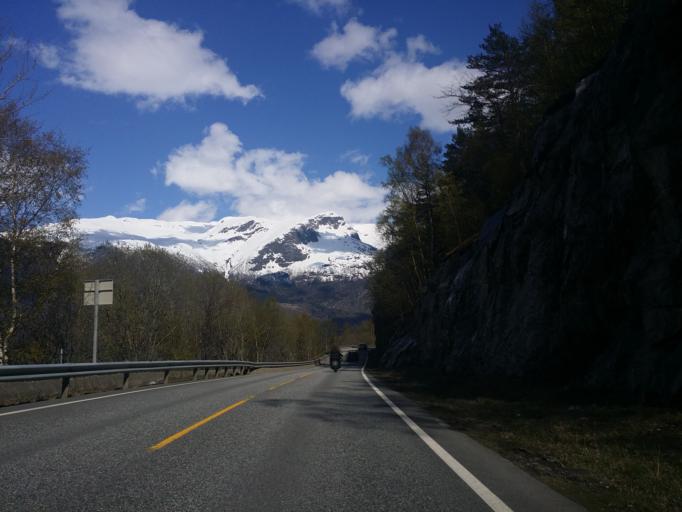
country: NO
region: Hordaland
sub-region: Ulvik
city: Ulvik
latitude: 60.4741
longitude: 6.9510
